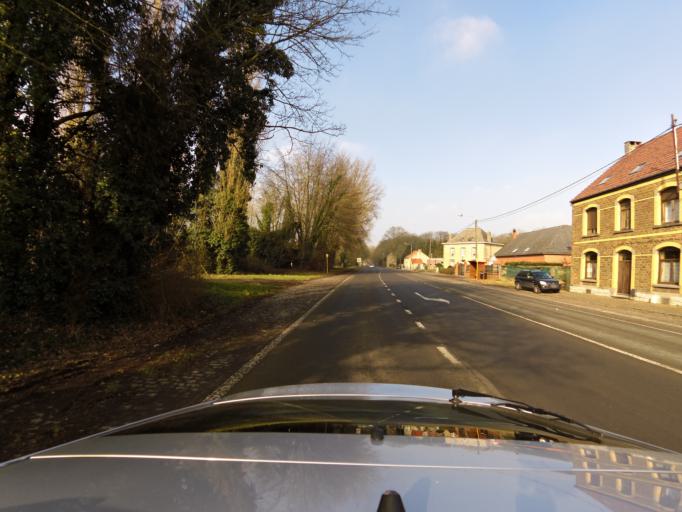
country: BE
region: Wallonia
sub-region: Province du Hainaut
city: Bernissart
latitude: 50.5057
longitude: 3.6932
